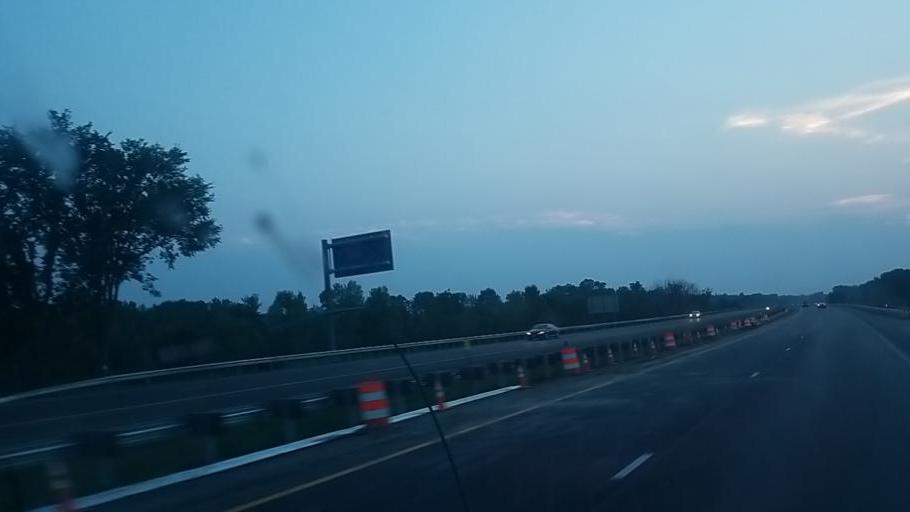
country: US
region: New York
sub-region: Oneida County
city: Clark Mills
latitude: 43.1272
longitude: -75.4249
